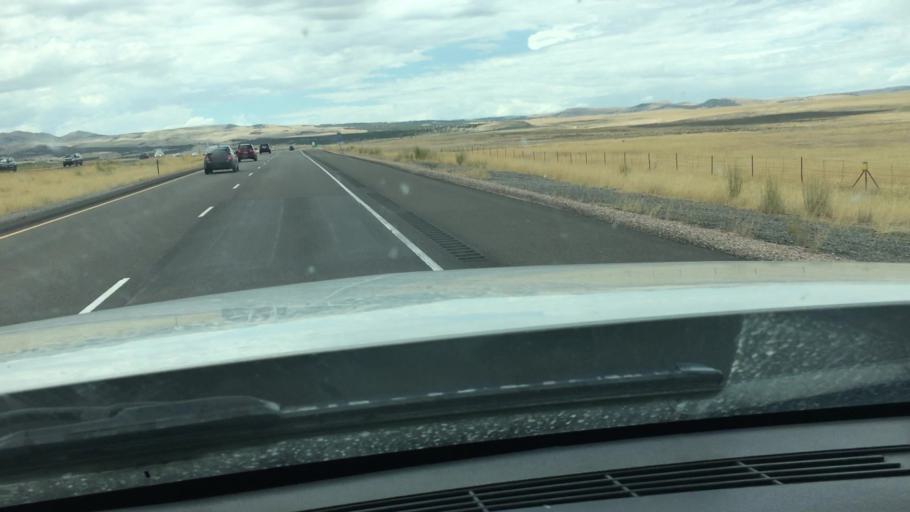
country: US
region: Utah
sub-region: Millard County
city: Fillmore
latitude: 38.7579
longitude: -112.5633
